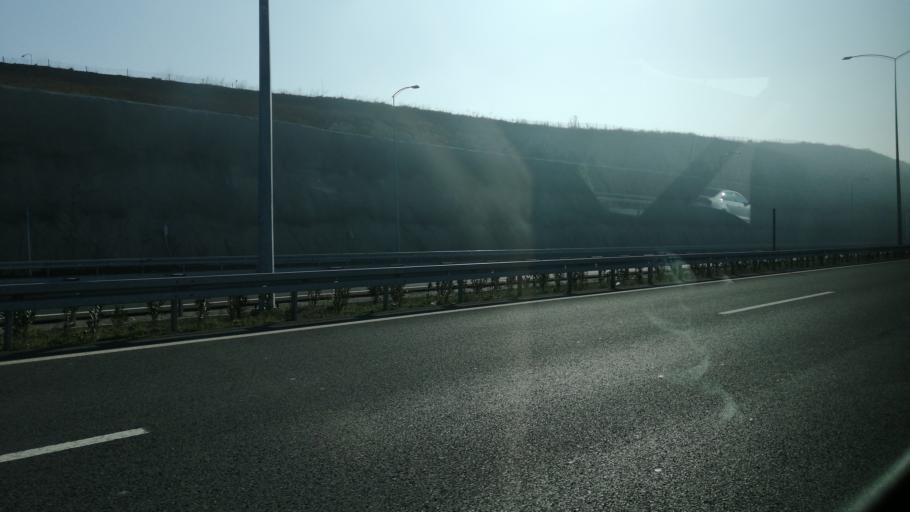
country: TR
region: Kocaeli
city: Tavsanli
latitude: 40.7810
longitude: 29.5172
